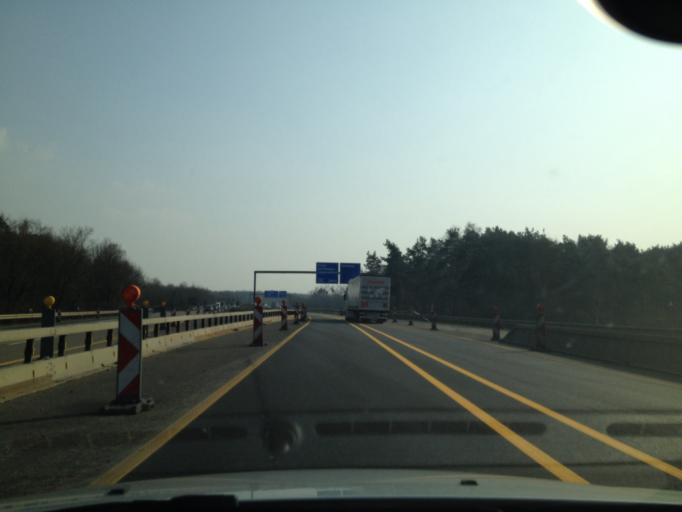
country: DE
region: Hesse
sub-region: Regierungsbezirk Darmstadt
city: Langenselbold
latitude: 50.1709
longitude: 9.0166
